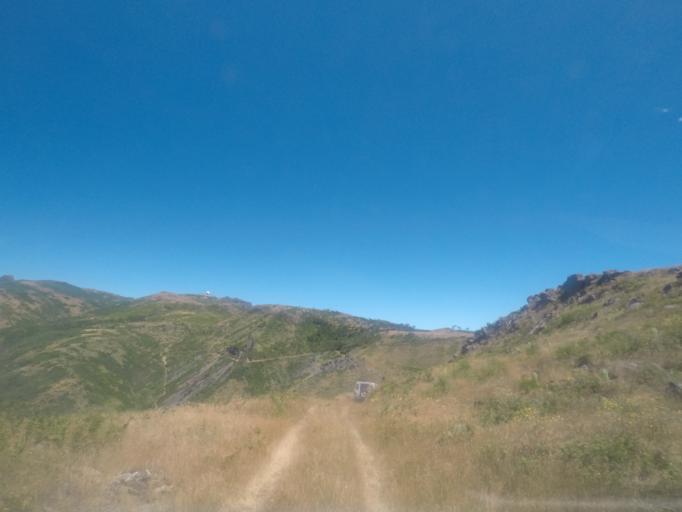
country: PT
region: Madeira
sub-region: Funchal
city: Nossa Senhora do Monte
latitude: 32.7112
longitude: -16.9139
